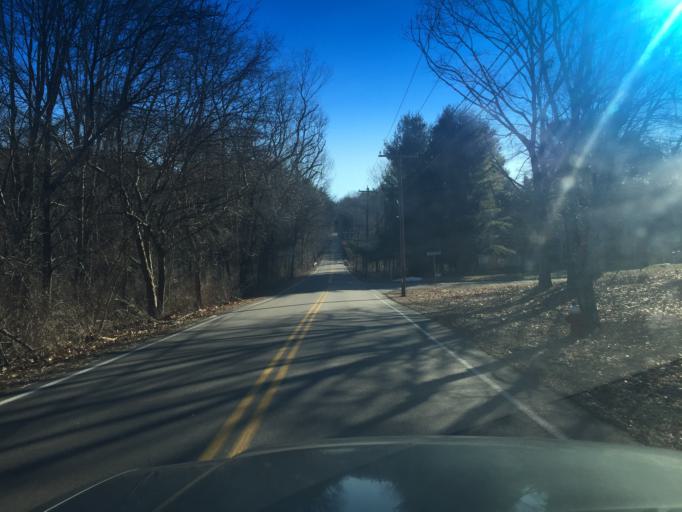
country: US
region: Massachusetts
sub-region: Middlesex County
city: Holliston
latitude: 42.1959
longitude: -71.3929
